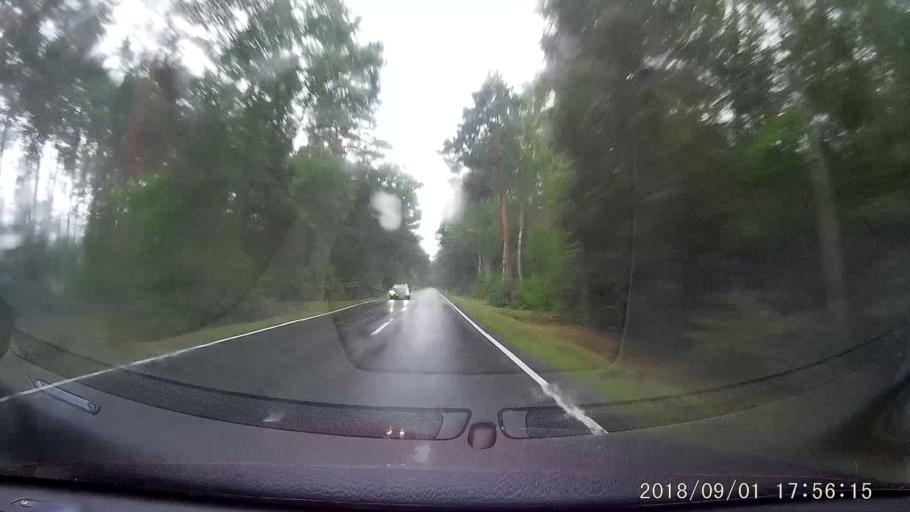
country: PL
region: Lubusz
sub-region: Powiat zaganski
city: Ilowa
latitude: 51.4475
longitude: 15.1985
